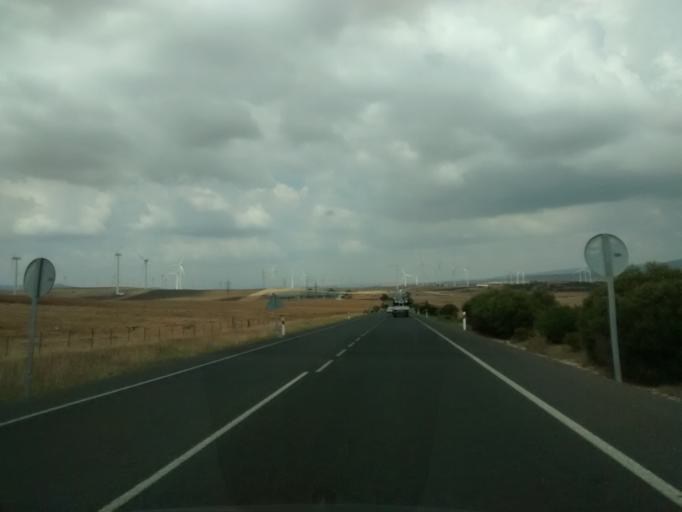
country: ES
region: Andalusia
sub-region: Provincia de Cadiz
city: Zahara de los Atunes
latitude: 36.1376
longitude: -5.7118
